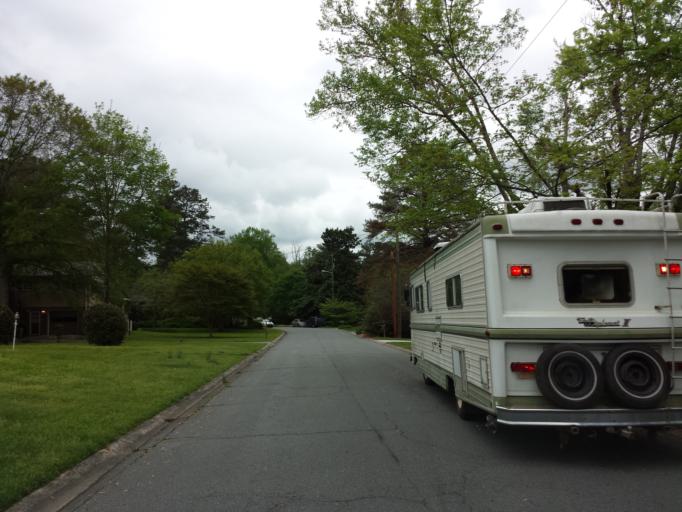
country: US
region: Georgia
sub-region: Cobb County
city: Marietta
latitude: 33.9452
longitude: -84.5715
